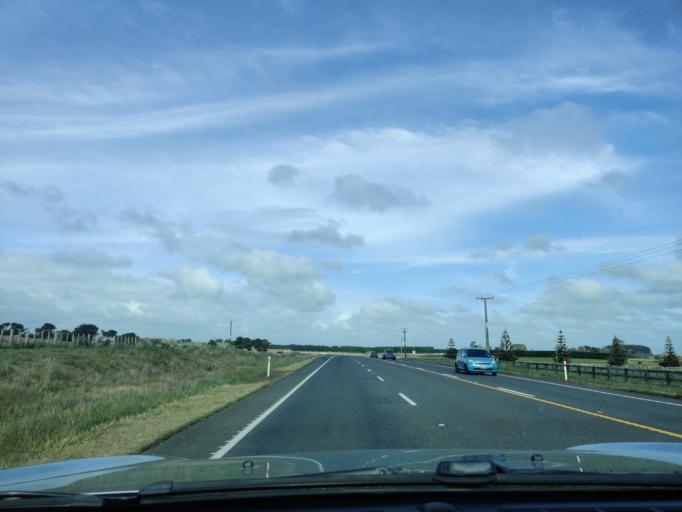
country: NZ
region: Manawatu-Wanganui
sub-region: Wanganui District
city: Wanganui
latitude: -39.9815
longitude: 175.1468
